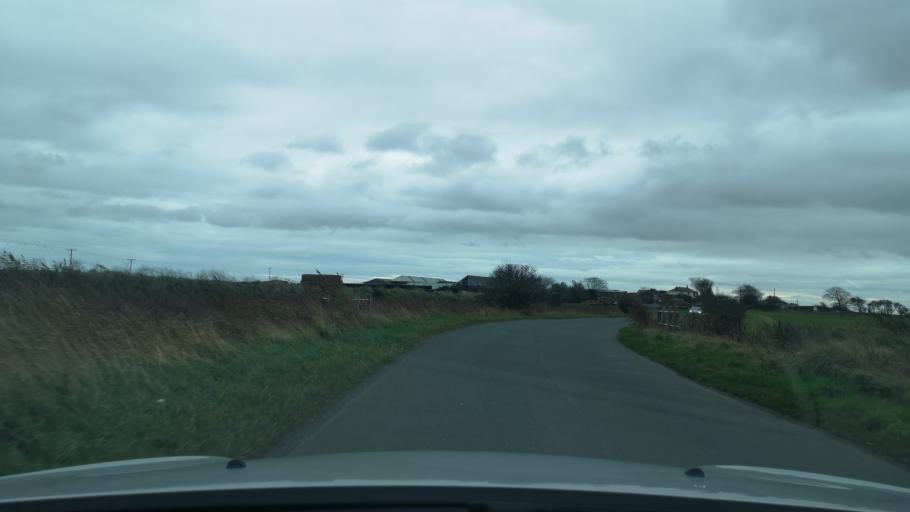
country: GB
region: England
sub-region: East Riding of Yorkshire
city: Easington
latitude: 53.6280
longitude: 0.1247
